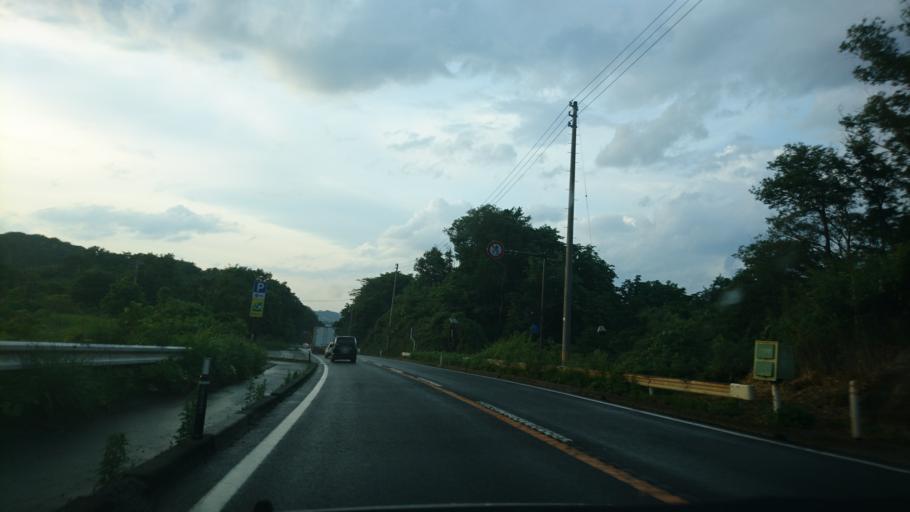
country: JP
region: Iwate
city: Ichinoseki
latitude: 38.9577
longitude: 141.1226
